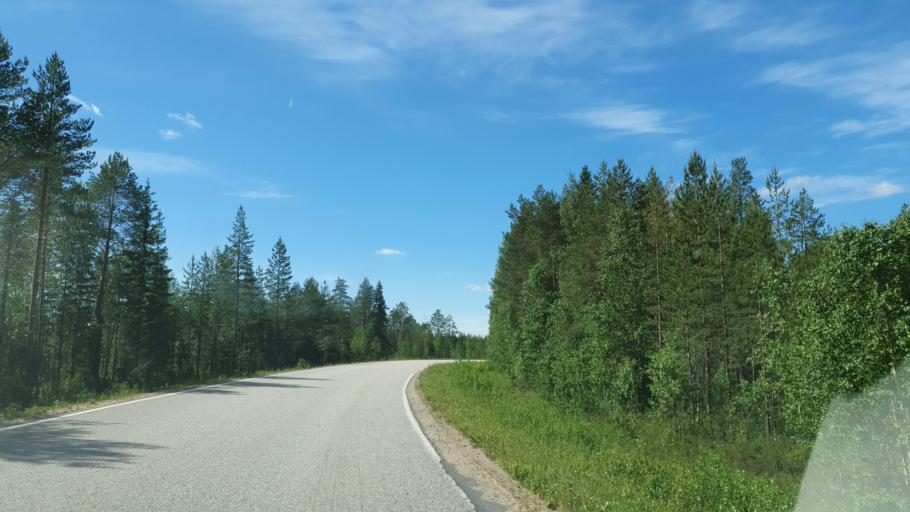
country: FI
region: Kainuu
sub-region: Kehys-Kainuu
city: Suomussalmi
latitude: 64.5749
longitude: 29.0283
